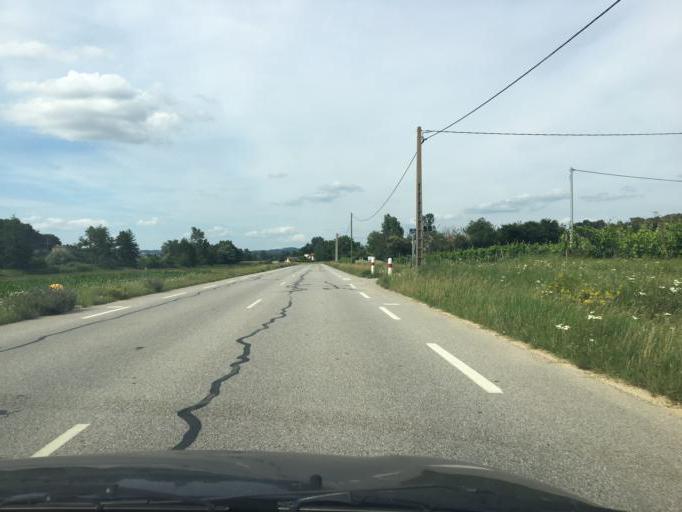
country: FR
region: Rhone-Alpes
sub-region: Departement de la Drome
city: Chanos-Curson
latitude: 45.0623
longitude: 4.9308
